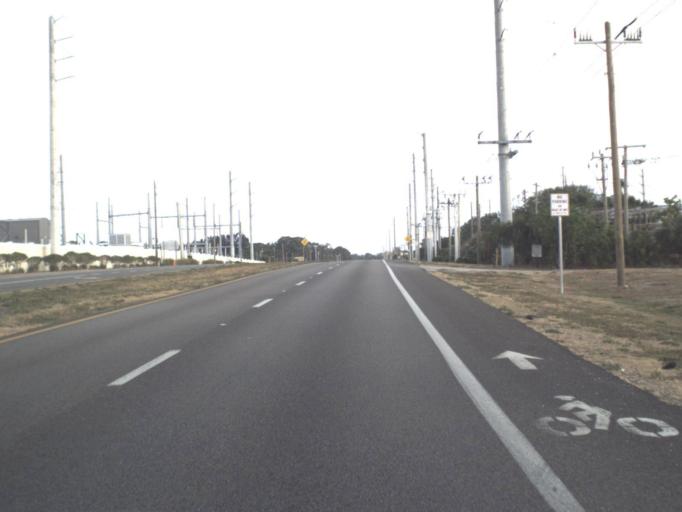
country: US
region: Florida
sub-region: Brevard County
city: Port Saint John
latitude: 28.4714
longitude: -80.7667
